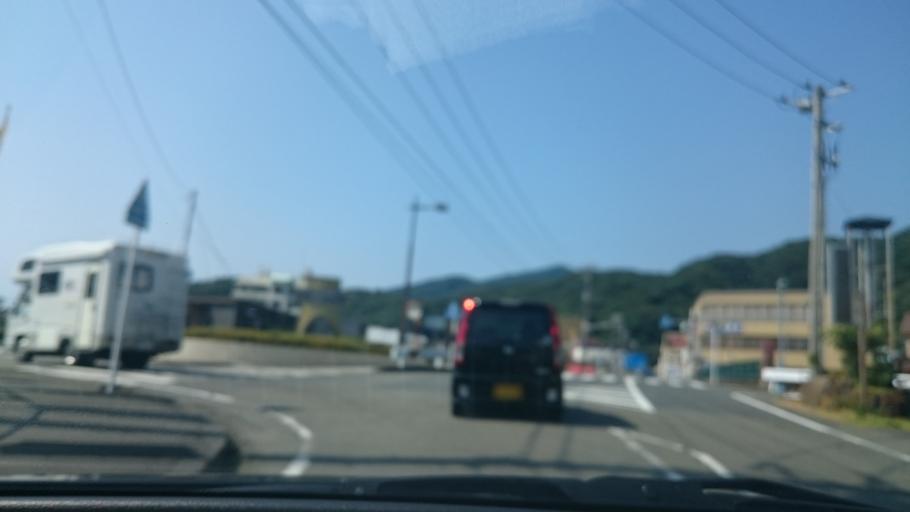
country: JP
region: Shizuoka
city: Heda
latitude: 34.9106
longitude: 138.7915
